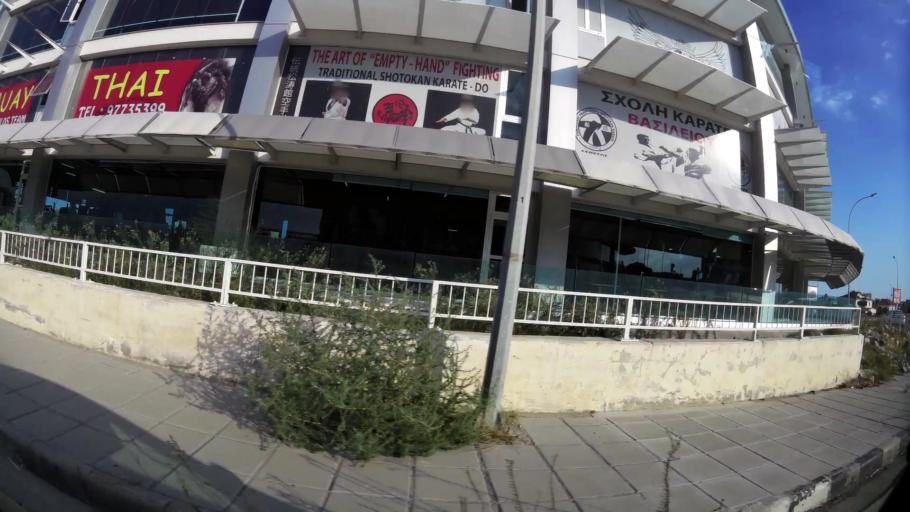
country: CY
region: Larnaka
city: Larnaca
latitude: 34.9289
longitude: 33.6043
